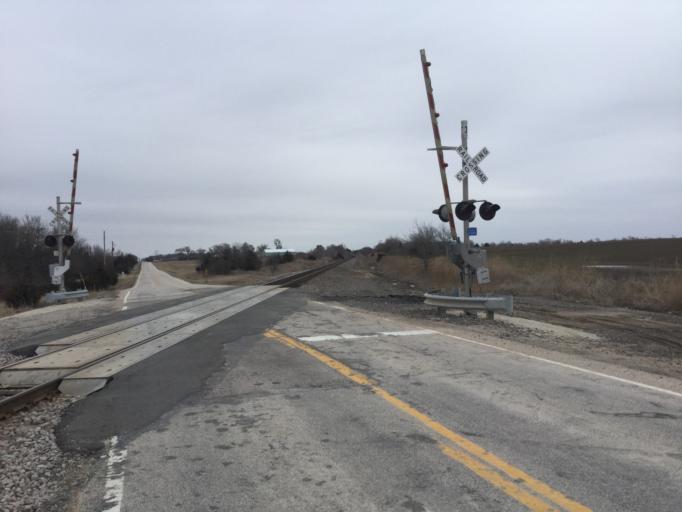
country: US
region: Kansas
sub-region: Sumner County
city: Mulvane
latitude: 37.5106
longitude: -97.2081
